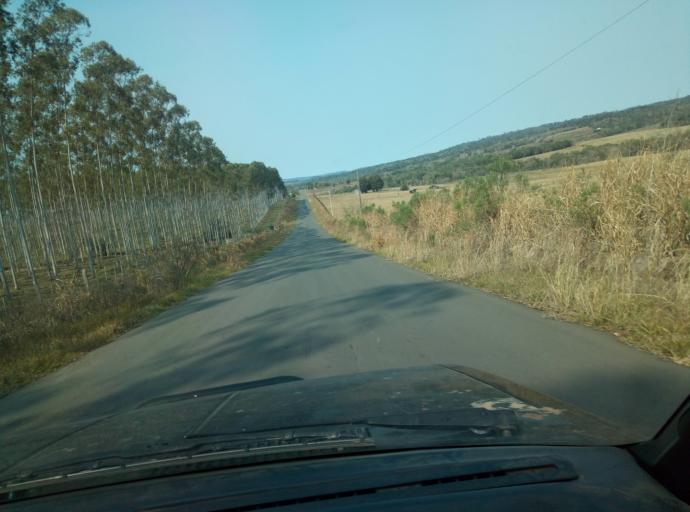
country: PY
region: Caaguazu
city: Carayao
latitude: -25.2524
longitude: -56.2880
